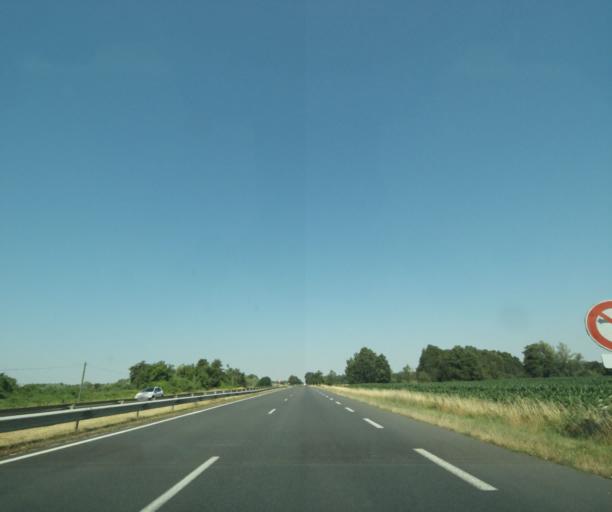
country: FR
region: Champagne-Ardenne
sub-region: Departement de la Haute-Marne
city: Villiers-en-Lieu
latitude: 48.6670
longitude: 4.7883
